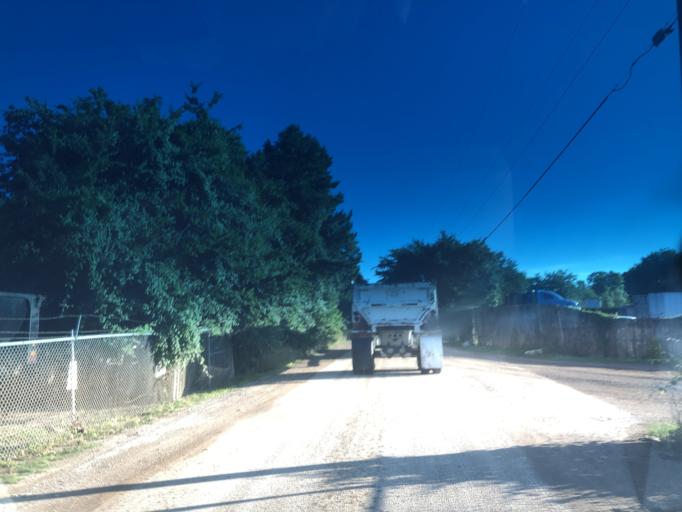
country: US
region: Texas
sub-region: Dallas County
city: Grand Prairie
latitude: 32.7897
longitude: -97.0091
